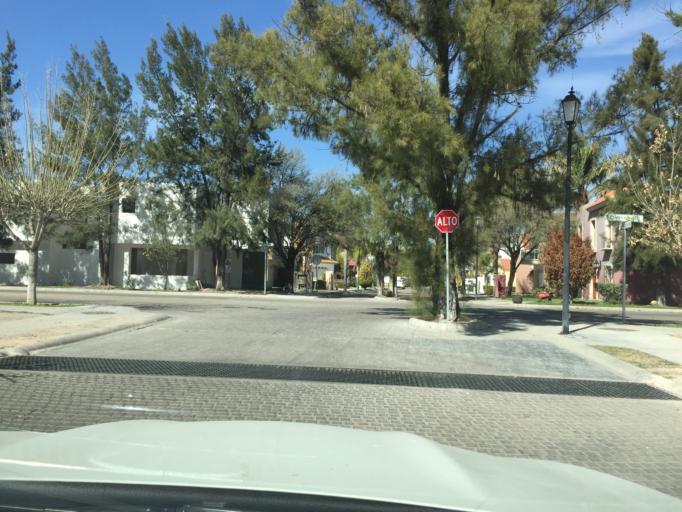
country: MX
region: Aguascalientes
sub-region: Aguascalientes
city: La Loma de los Negritos
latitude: 21.8504
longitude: -102.3555
